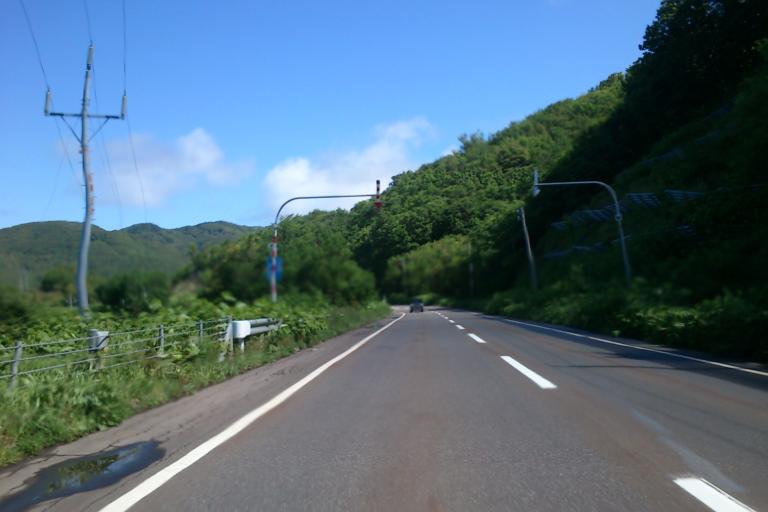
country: JP
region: Hokkaido
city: Ishikari
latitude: 43.5007
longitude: 141.3738
